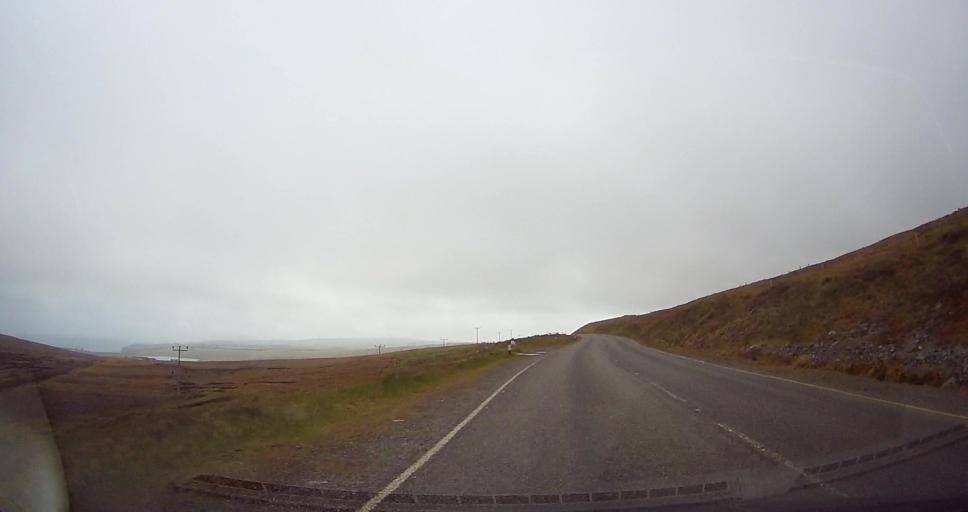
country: GB
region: Scotland
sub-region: Shetland Islands
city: Sandwick
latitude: 59.9596
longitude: -1.2843
